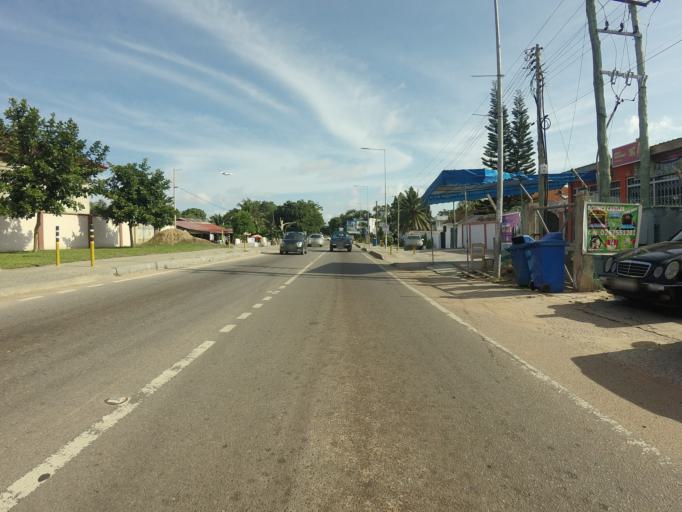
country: GH
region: Greater Accra
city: Medina Estates
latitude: 5.6313
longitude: -0.1608
